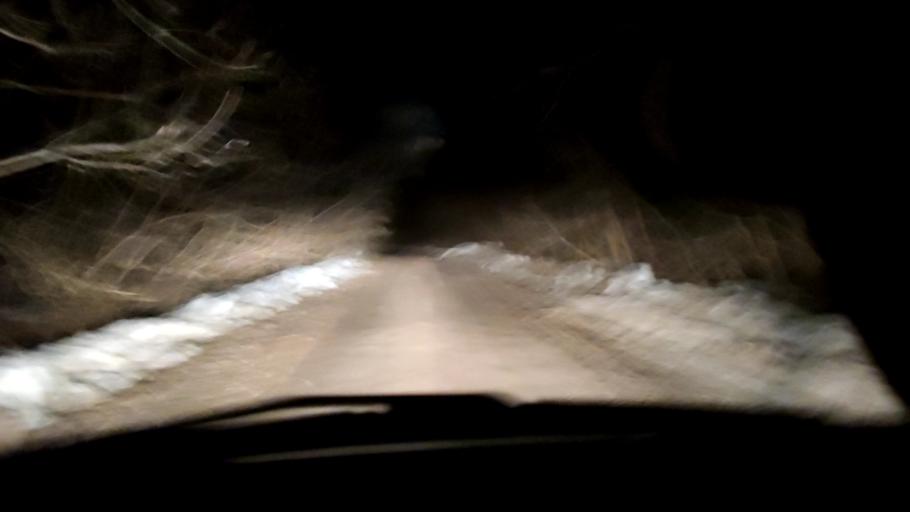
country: RU
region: Bashkortostan
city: Ufa
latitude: 54.7679
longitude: 56.1447
